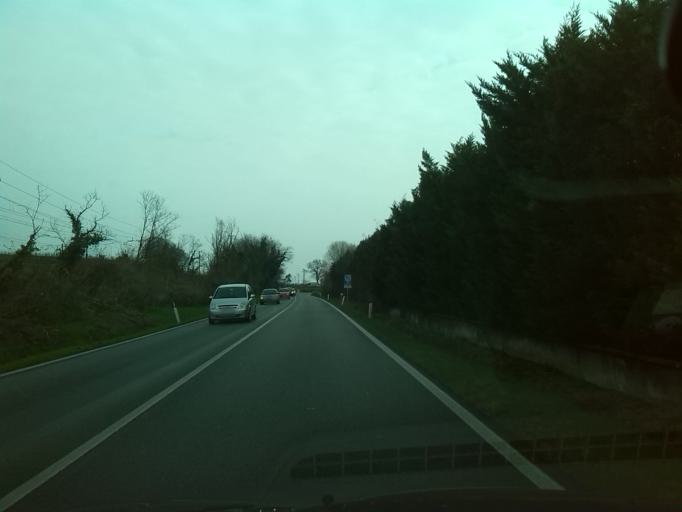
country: IT
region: Friuli Venezia Giulia
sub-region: Provincia di Gorizia
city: Moraro
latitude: 45.9451
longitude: 13.4894
